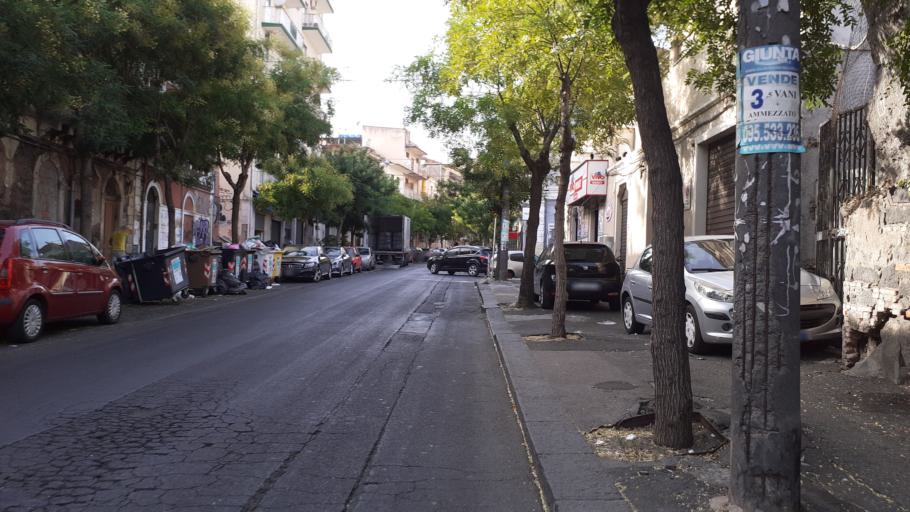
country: IT
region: Sicily
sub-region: Catania
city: Catania
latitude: 37.5020
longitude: 15.0753
